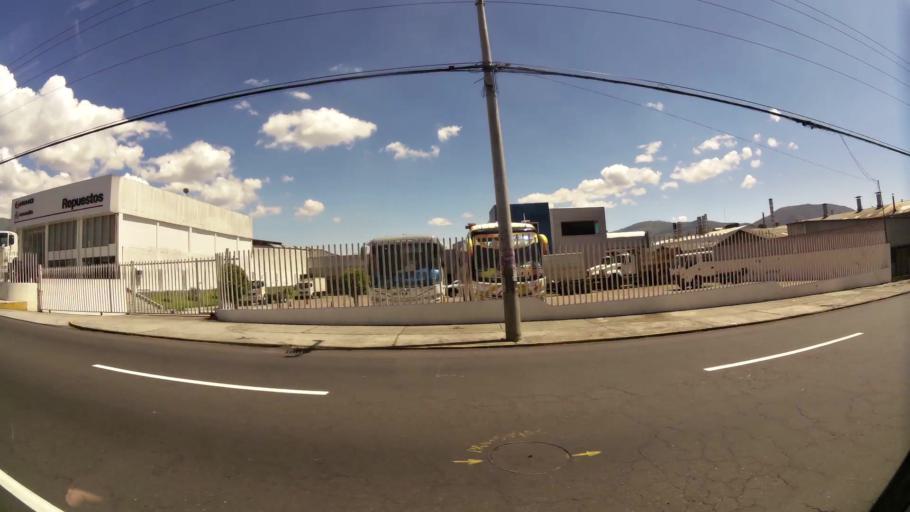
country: EC
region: Pichincha
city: Quito
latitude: -0.1059
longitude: -78.4761
